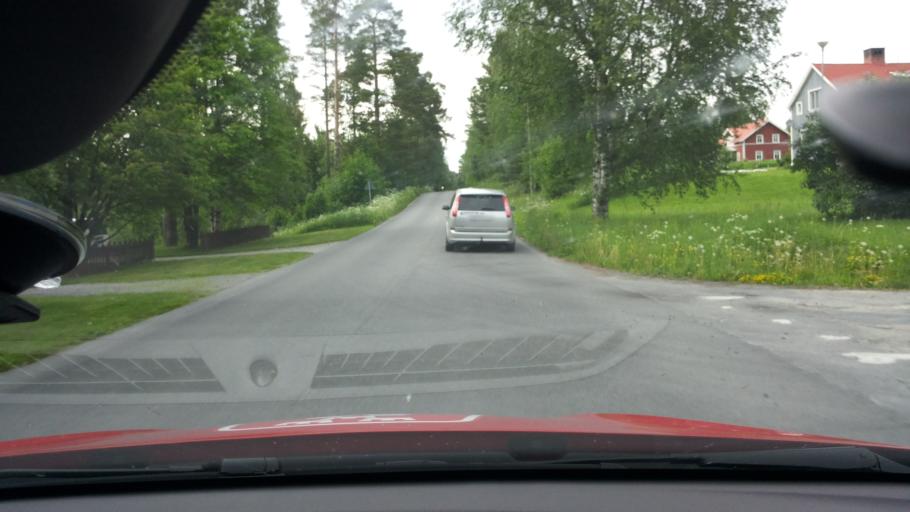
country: SE
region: Jaemtland
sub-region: Bergs Kommun
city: Hoverberg
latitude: 62.9281
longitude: 14.5160
